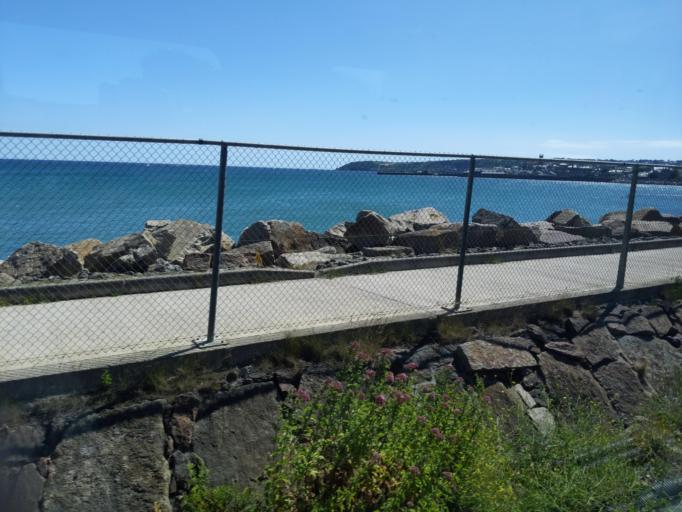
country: GB
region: England
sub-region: Cornwall
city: Penzance
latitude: 50.1262
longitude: -5.5249
